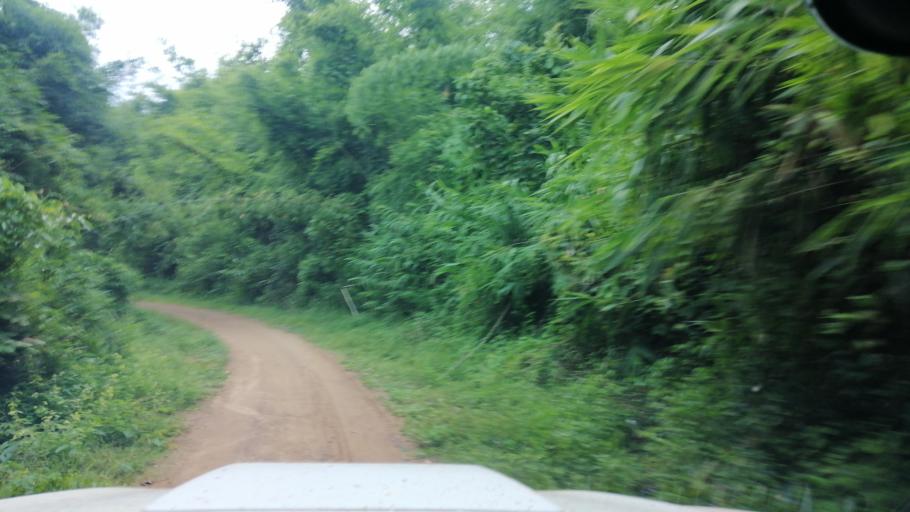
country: TH
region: Nan
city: Mae Charim
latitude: 18.7480
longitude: 101.2871
